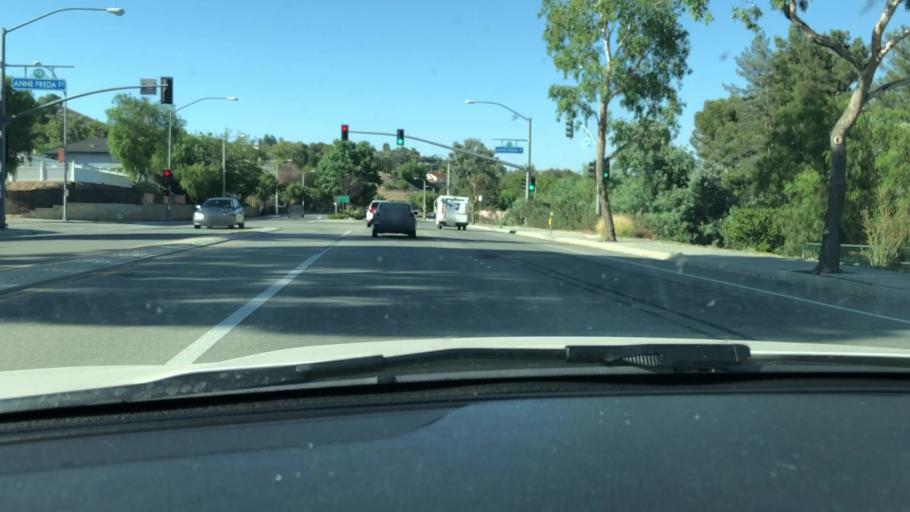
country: US
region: California
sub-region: Los Angeles County
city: Santa Clarita
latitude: 34.4226
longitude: -118.4332
